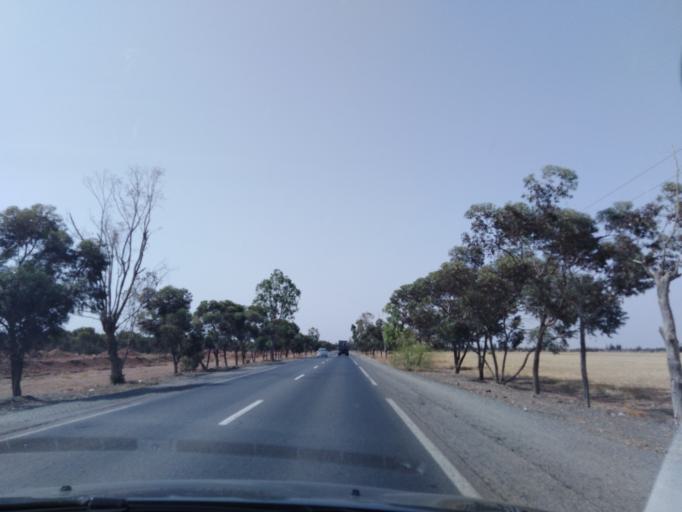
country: MA
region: Marrakech-Tensift-Al Haouz
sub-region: Kelaa-Des-Sraghna
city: Sidi Bou Othmane
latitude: 31.9537
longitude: -7.9466
